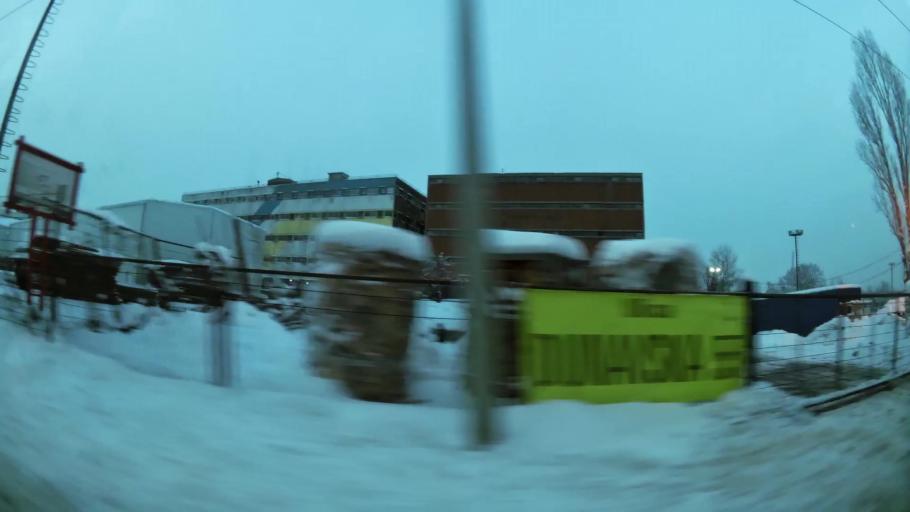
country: RS
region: Central Serbia
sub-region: Belgrade
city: Stari Grad
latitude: 44.8214
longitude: 20.4808
